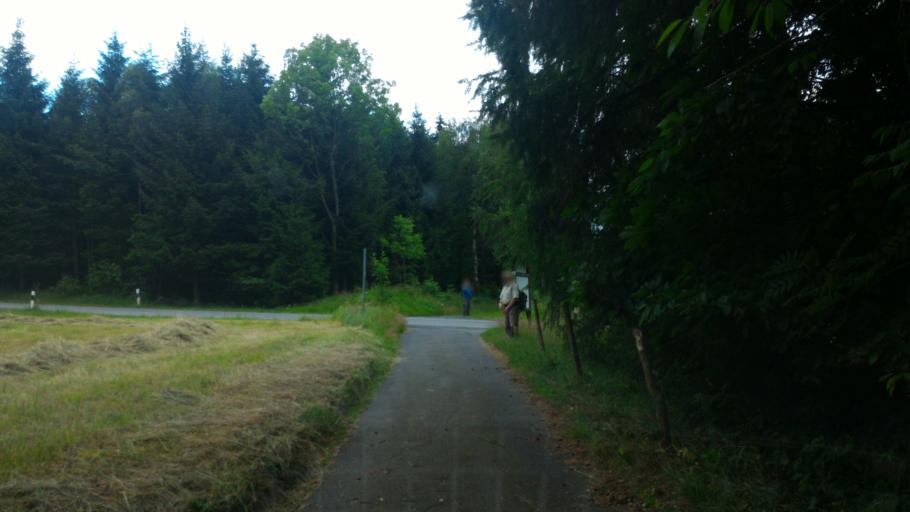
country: DE
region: Saxony
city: Kurort Jonsdorf
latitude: 50.8428
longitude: 14.7085
